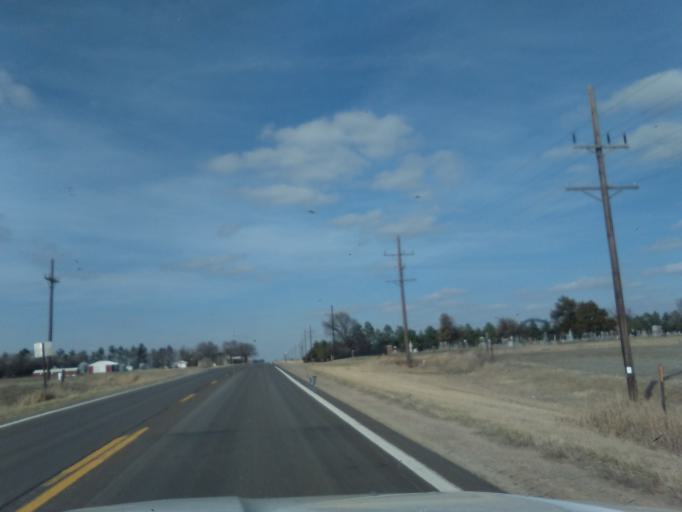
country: US
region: Nebraska
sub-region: Gage County
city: Beatrice
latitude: 40.1314
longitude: -96.9354
